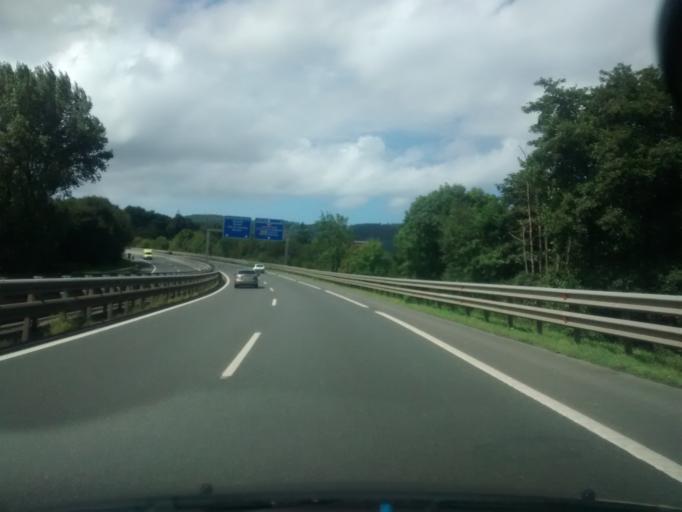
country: ES
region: Basque Country
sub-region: Provincia de Guipuzcoa
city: San Sebastian
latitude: 43.2984
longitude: -2.0025
